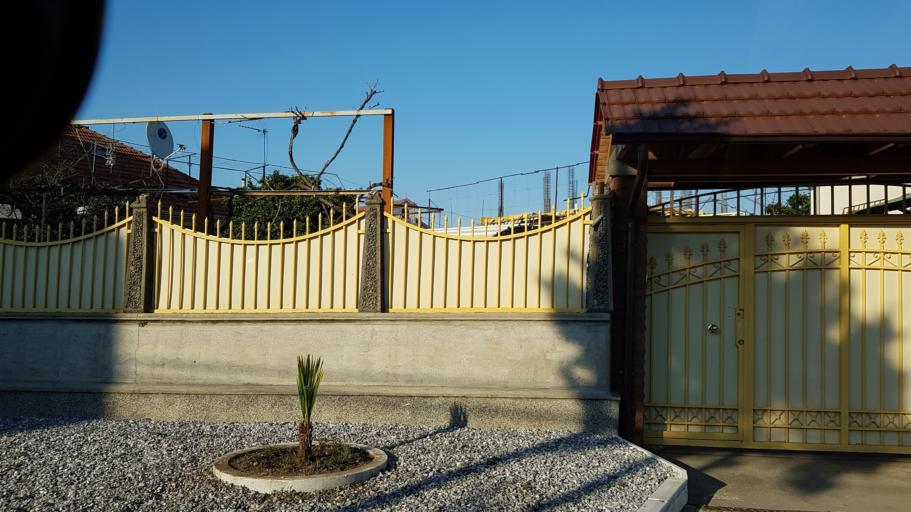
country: AL
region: Shkoder
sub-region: Rrethi i Shkodres
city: Shkoder
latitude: 42.0772
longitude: 19.5024
